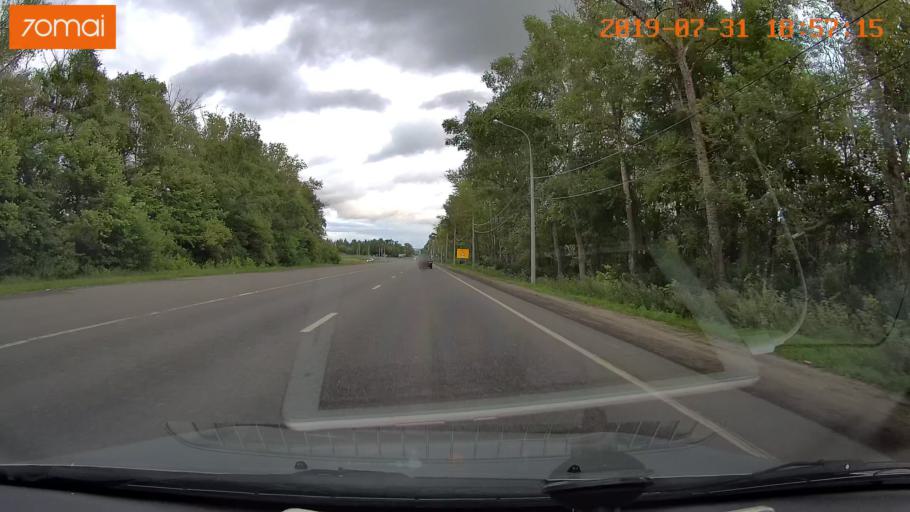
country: RU
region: Moskovskaya
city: Raduzhnyy
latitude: 55.1556
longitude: 38.6897
